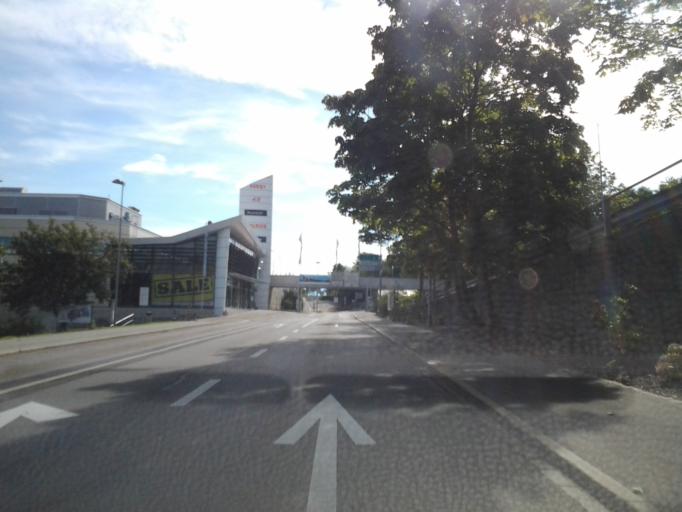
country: CH
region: Schwyz
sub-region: Bezirk Hoefe
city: Freienbach
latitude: 47.2000
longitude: 8.7916
